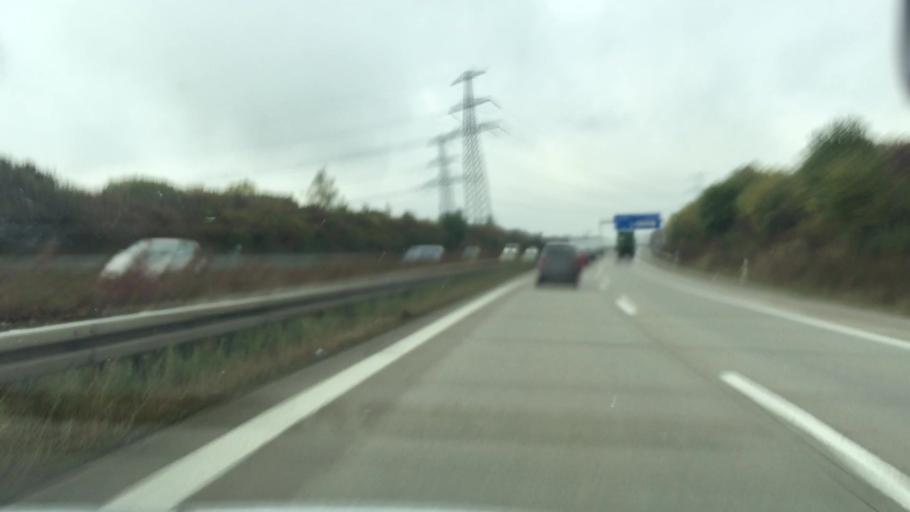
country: DE
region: Saxony
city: Hartmannsdorf
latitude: 50.8598
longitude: 12.8190
